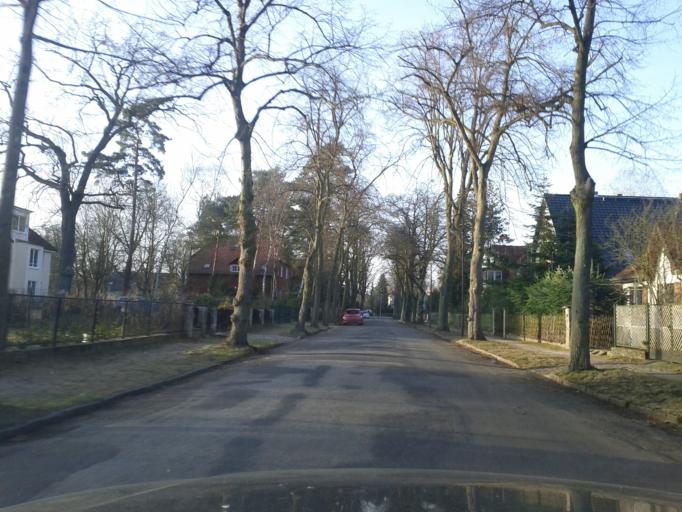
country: DE
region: Brandenburg
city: Schoneiche
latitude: 52.4719
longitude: 13.6893
